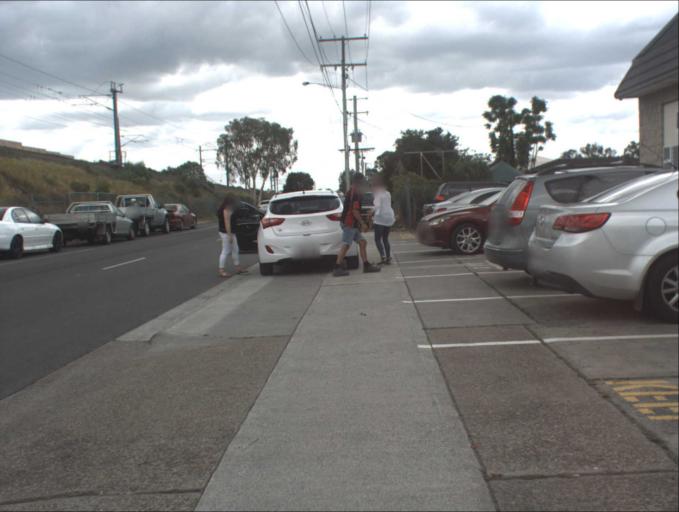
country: AU
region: Queensland
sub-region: Logan
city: Beenleigh
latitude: -27.7144
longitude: 153.1929
